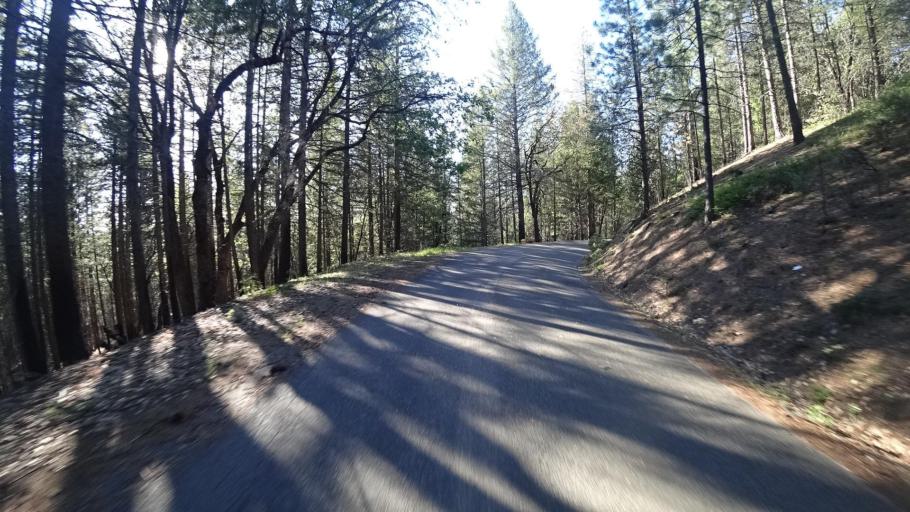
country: US
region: California
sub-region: Lake County
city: Upper Lake
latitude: 39.3015
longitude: -122.9300
